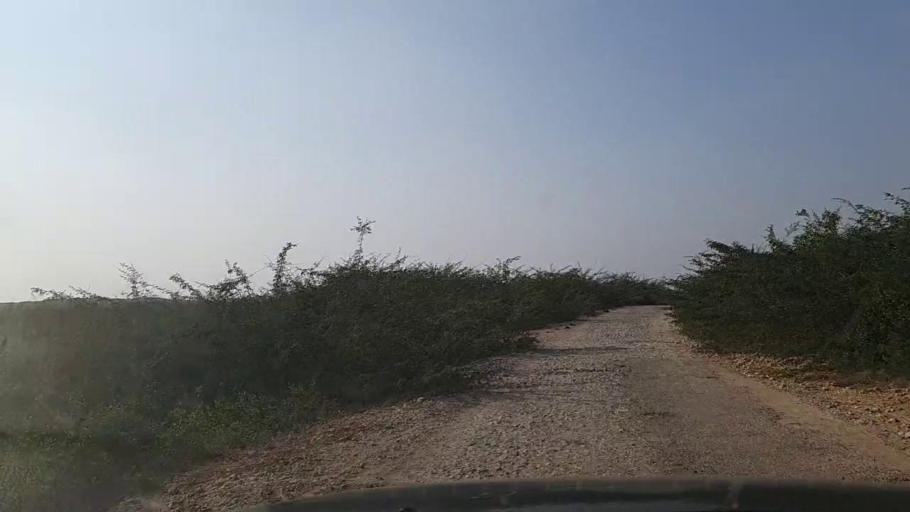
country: PK
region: Sindh
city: Gharo
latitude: 24.7547
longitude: 67.5311
